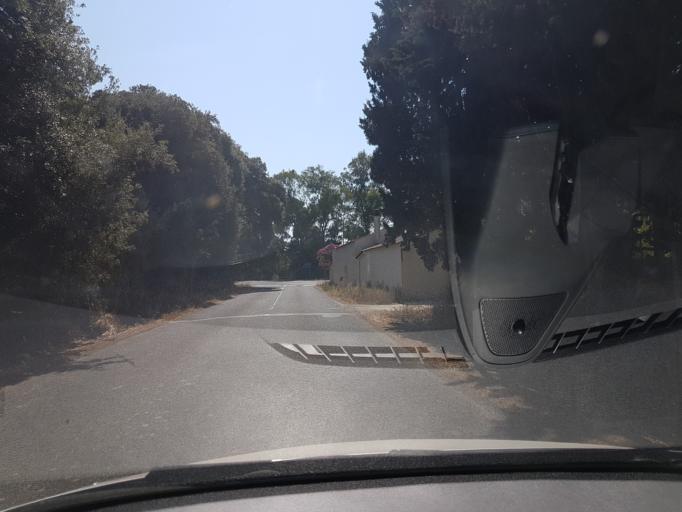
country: IT
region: Sardinia
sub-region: Provincia di Oristano
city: Solanas
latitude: 39.9214
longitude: 8.5650
